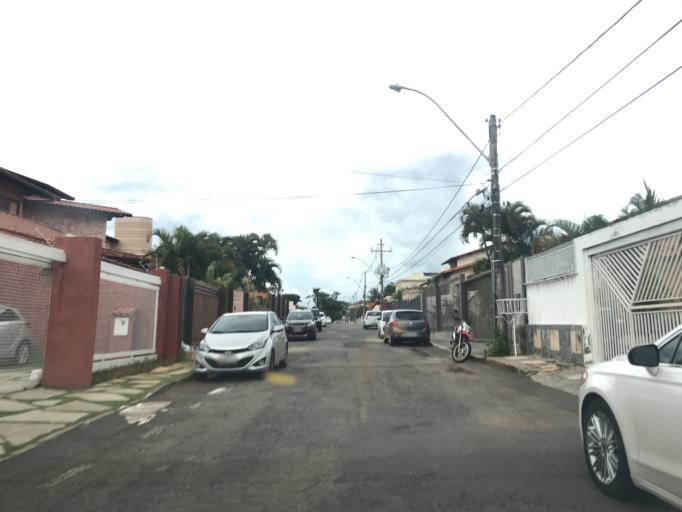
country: BR
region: Federal District
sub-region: Brasilia
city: Brasilia
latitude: -15.7213
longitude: -47.8785
